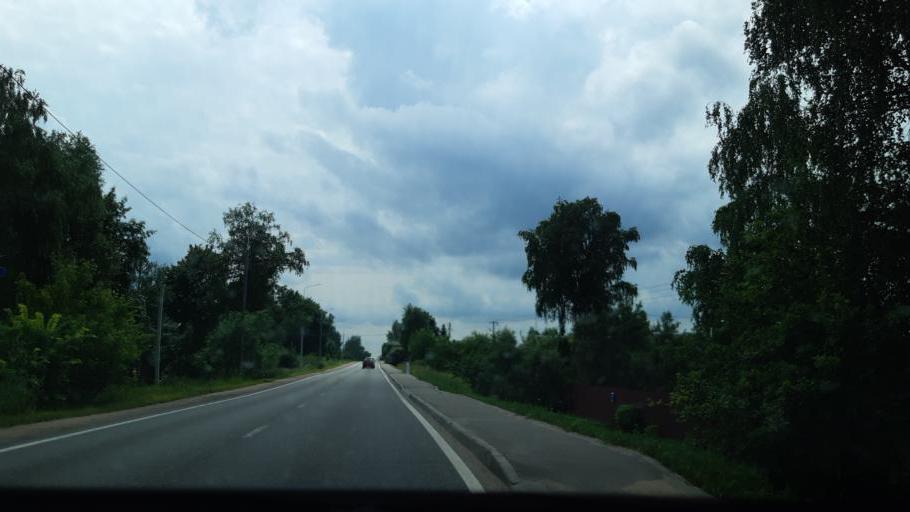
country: RU
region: Moskovskaya
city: Dorokhovo
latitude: 55.5392
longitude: 36.3655
